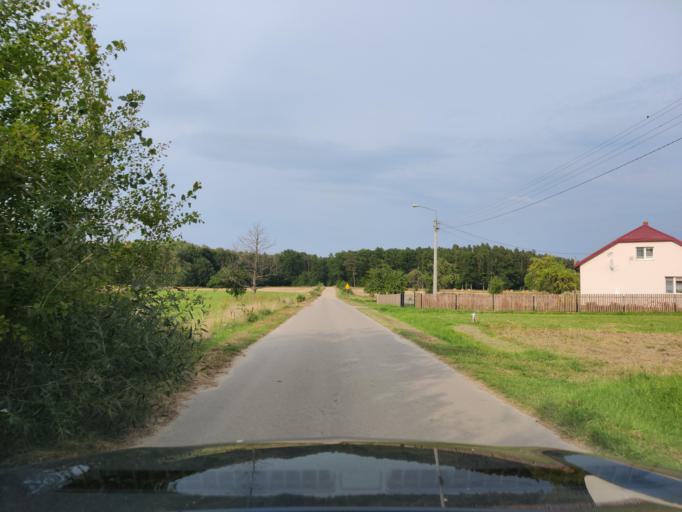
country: PL
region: Masovian Voivodeship
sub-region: Powiat pultuski
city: Obryte
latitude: 52.6977
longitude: 21.2057
